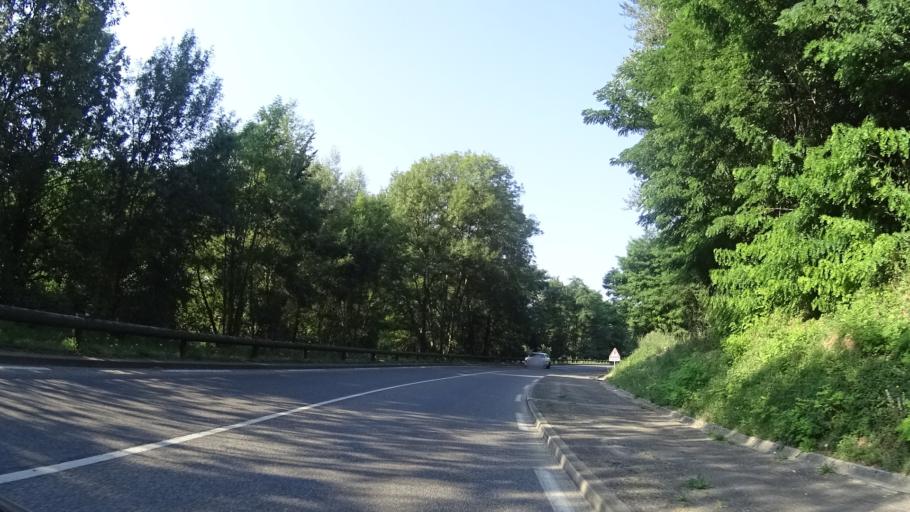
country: FR
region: Midi-Pyrenees
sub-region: Departement de l'Ariege
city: Lavelanet
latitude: 42.9574
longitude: 1.8631
